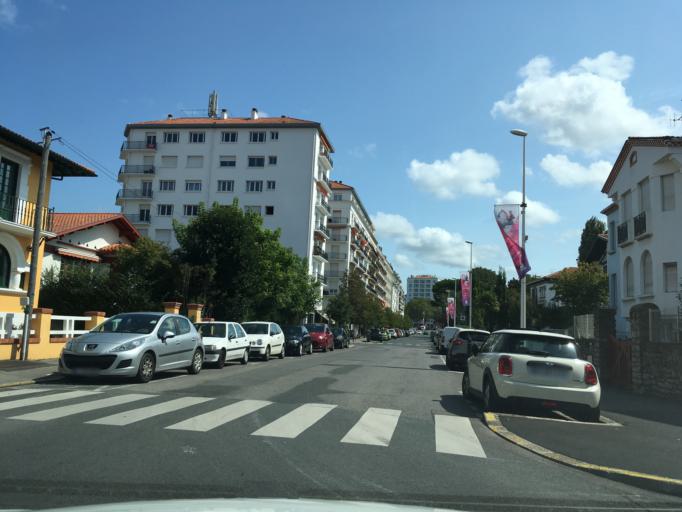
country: FR
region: Aquitaine
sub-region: Departement des Pyrenees-Atlantiques
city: Bayonne
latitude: 43.4943
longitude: -1.4838
